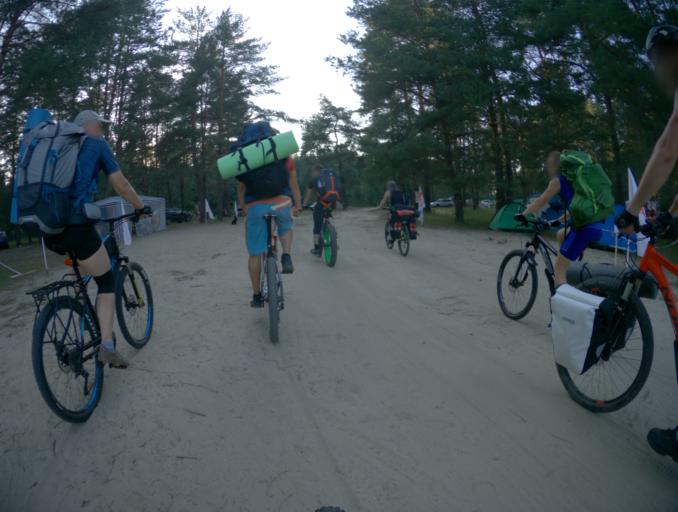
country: RU
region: Nizjnij Novgorod
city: Sitniki
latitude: 56.4616
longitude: 44.0137
